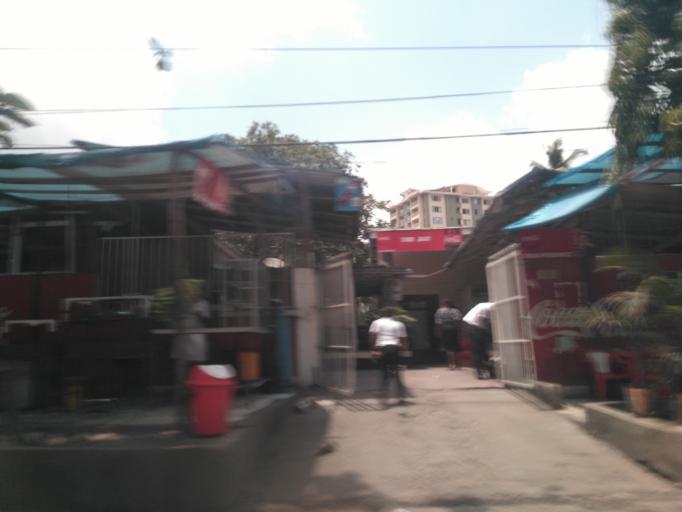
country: TZ
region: Dar es Salaam
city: Dar es Salaam
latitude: -6.8054
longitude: 39.2753
